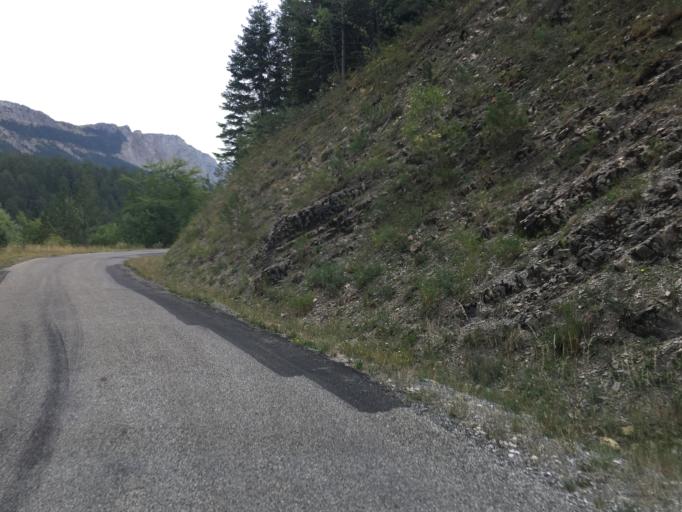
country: FR
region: Provence-Alpes-Cote d'Azur
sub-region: Departement des Alpes-de-Haute-Provence
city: Digne-les-Bains
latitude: 44.2224
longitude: 6.1365
